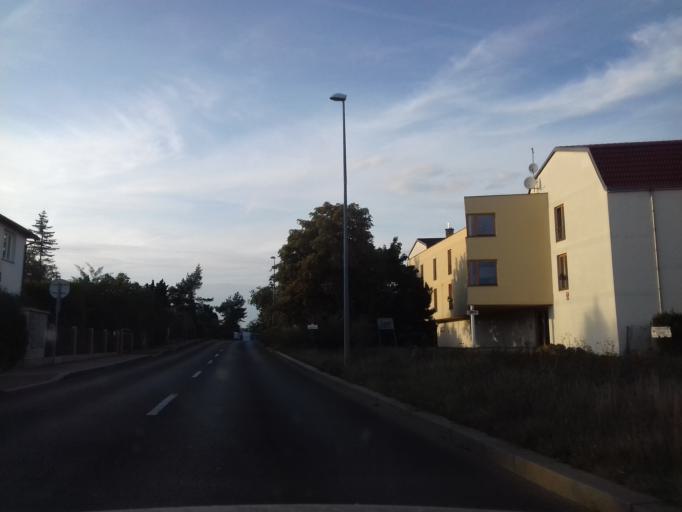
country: CZ
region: Praha
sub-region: Praha 4
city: Hodkovicky
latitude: 50.0148
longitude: 14.4561
